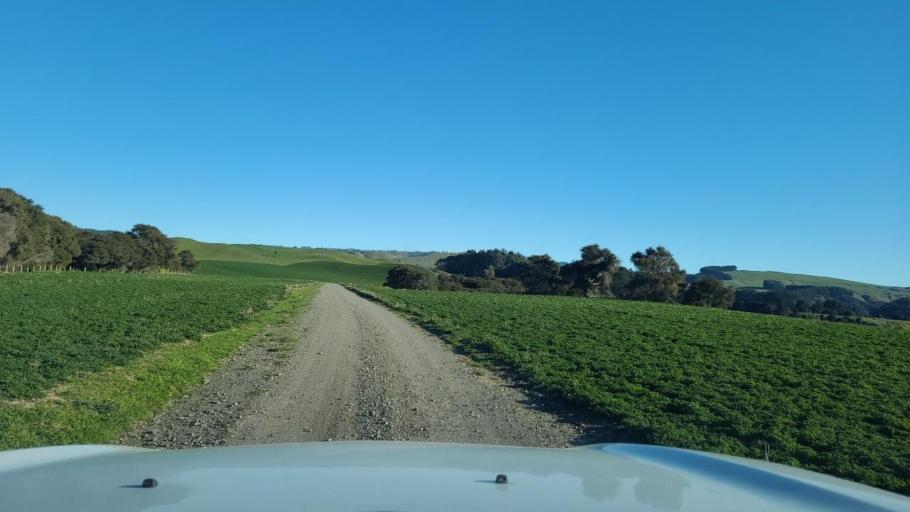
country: NZ
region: Hawke's Bay
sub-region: Napier City
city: Taradale
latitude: -39.4153
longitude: 176.5371
